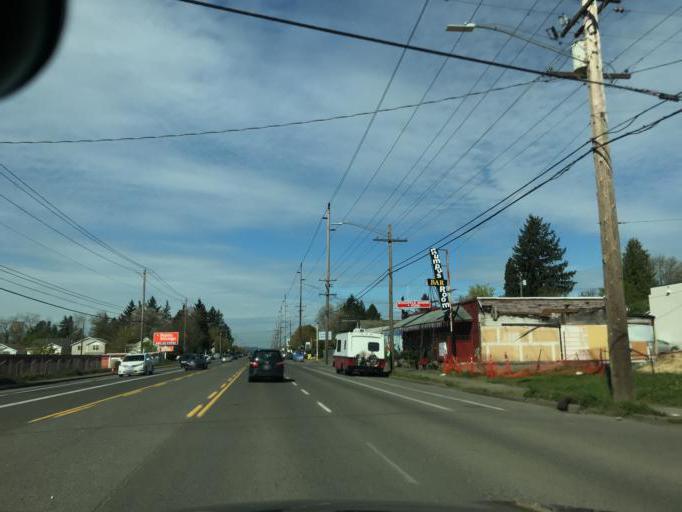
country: US
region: Oregon
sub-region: Multnomah County
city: Lents
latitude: 45.5043
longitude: -122.5537
